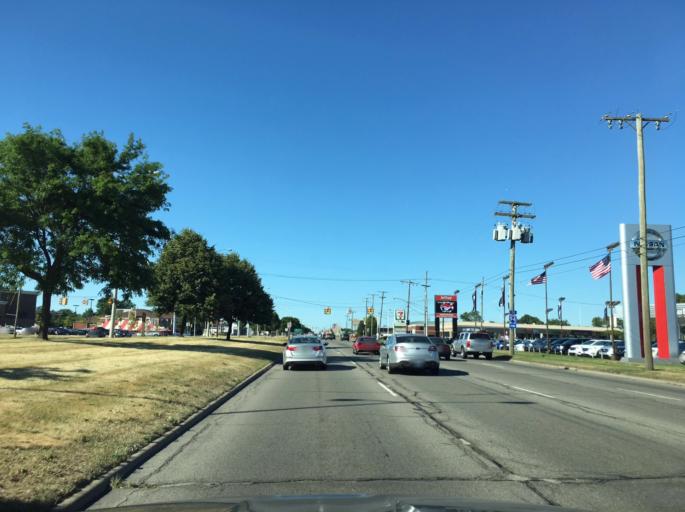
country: US
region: Michigan
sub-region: Macomb County
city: Roseville
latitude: 42.5239
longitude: -82.9192
